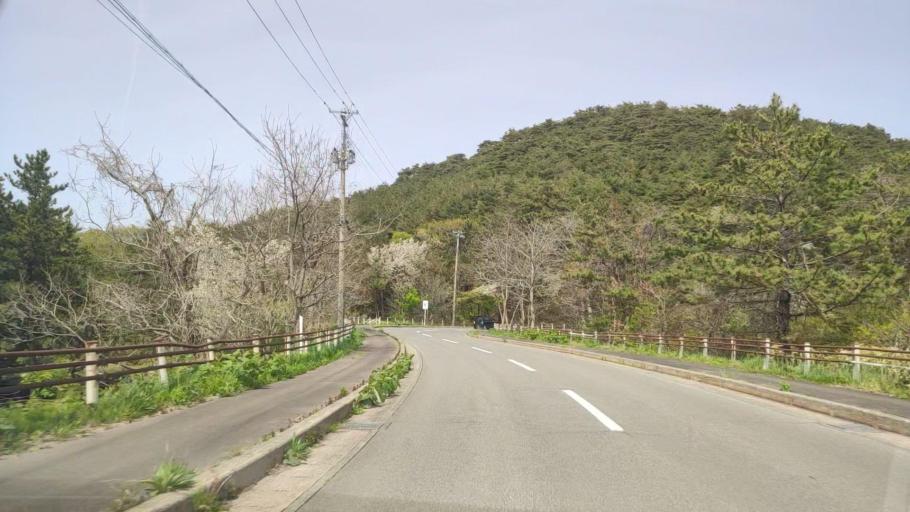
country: JP
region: Aomori
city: Aomori Shi
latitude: 40.9011
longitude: 140.8622
